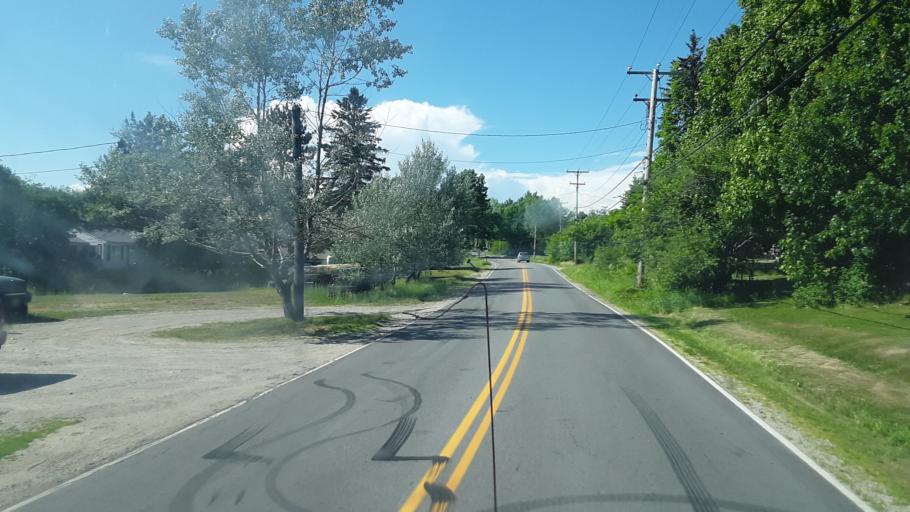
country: US
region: Maine
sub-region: Washington County
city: Cherryfield
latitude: 44.6119
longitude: -67.9243
